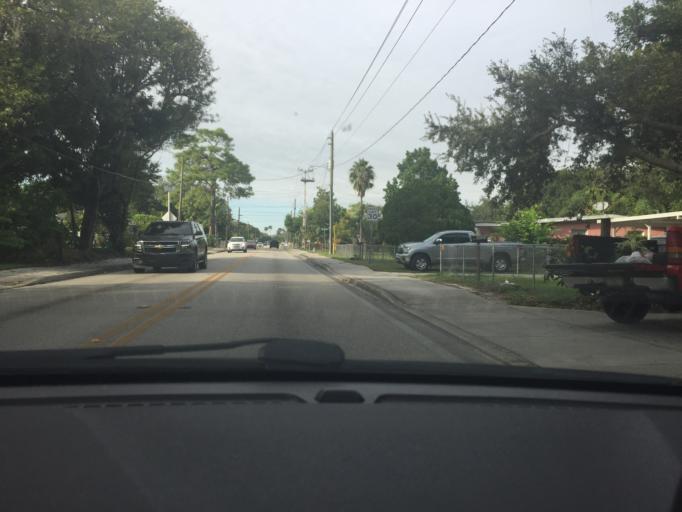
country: US
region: Florida
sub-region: Manatee County
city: Samoset
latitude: 27.4920
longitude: -82.5303
